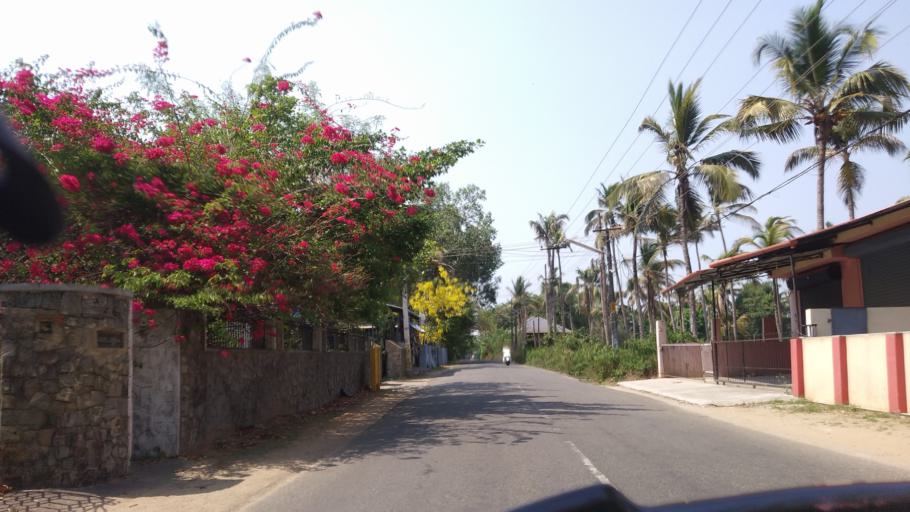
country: IN
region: Kerala
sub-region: Thrissur District
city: Kodungallur
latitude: 10.2590
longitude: 76.1453
